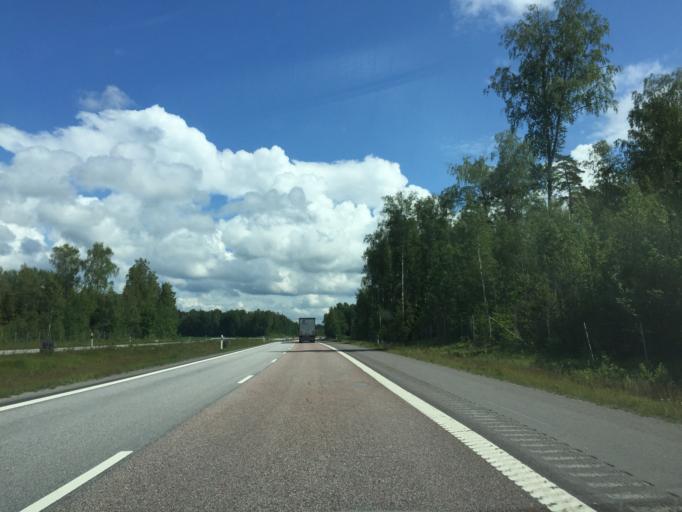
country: SE
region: OErebro
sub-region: Lindesbergs Kommun
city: Fellingsbro
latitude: 59.3192
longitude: 15.4724
